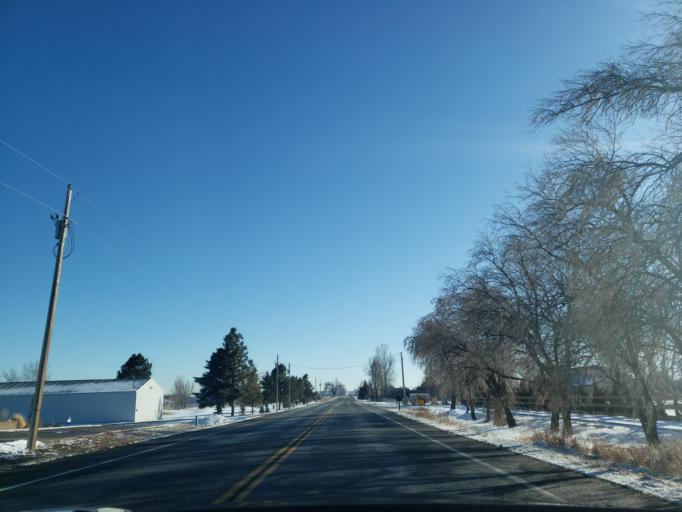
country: US
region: Colorado
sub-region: Weld County
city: Windsor
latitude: 40.5129
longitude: -105.0009
